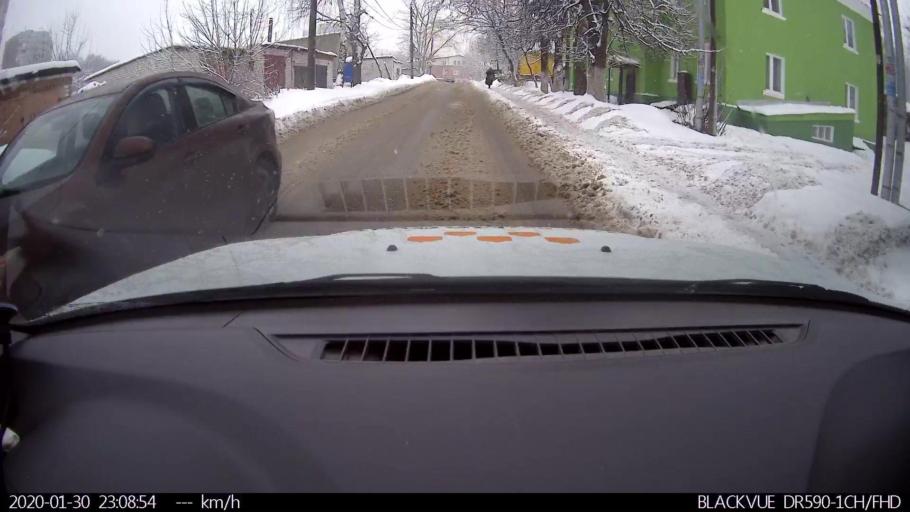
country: RU
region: Nizjnij Novgorod
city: Bor
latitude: 56.3115
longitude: 44.0541
